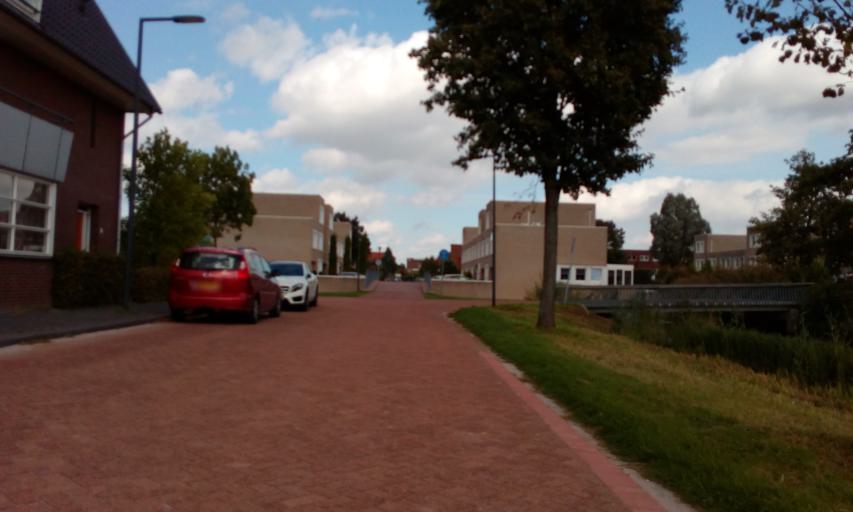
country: NL
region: South Holland
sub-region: Gemeente Capelle aan den IJssel
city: Capelle aan den IJssel
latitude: 51.9834
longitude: 4.5938
